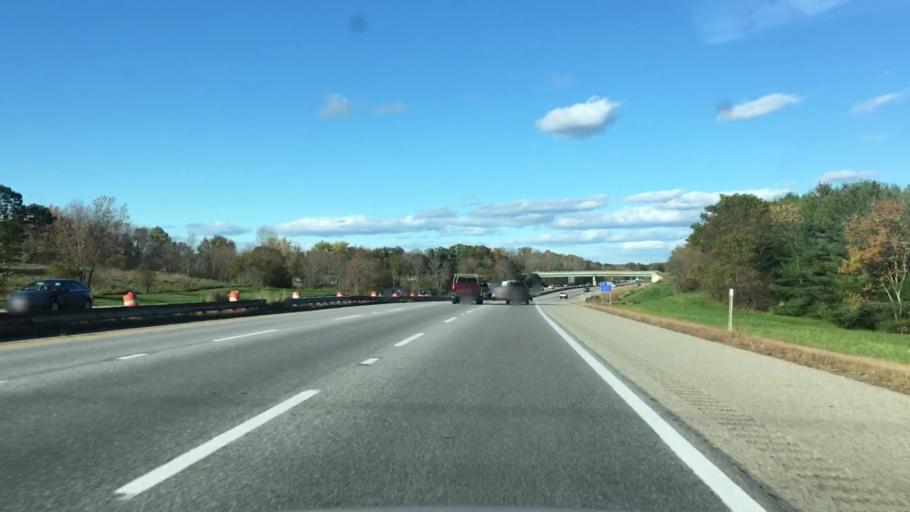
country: US
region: Maine
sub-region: York County
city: Biddeford
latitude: 43.4921
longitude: -70.4918
